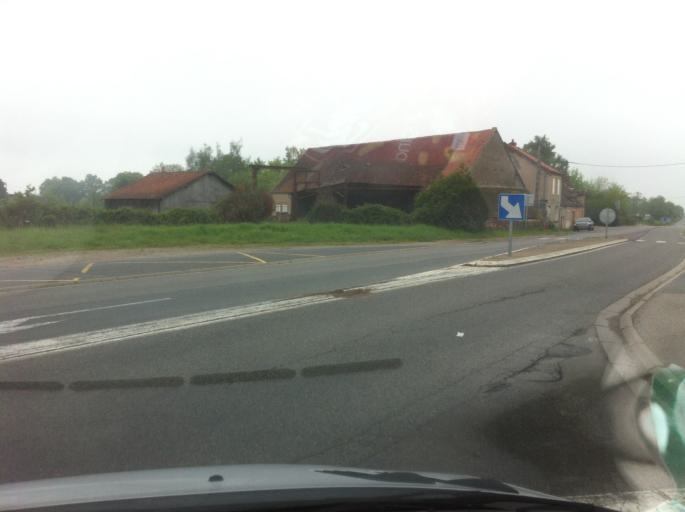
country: FR
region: Auvergne
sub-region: Departement de l'Allier
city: Montmarault
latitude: 46.3257
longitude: 3.0637
